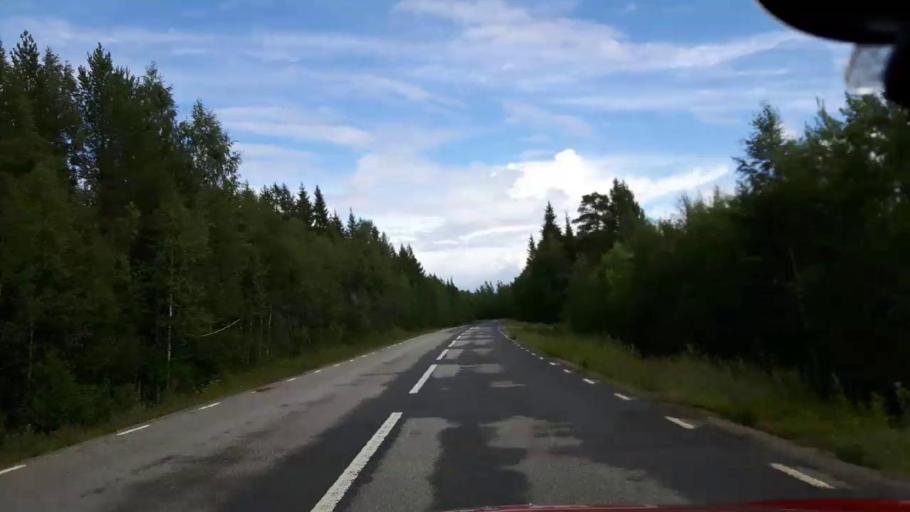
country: SE
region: Jaemtland
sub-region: Stroemsunds Kommun
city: Stroemsund
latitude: 64.3394
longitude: 15.0267
